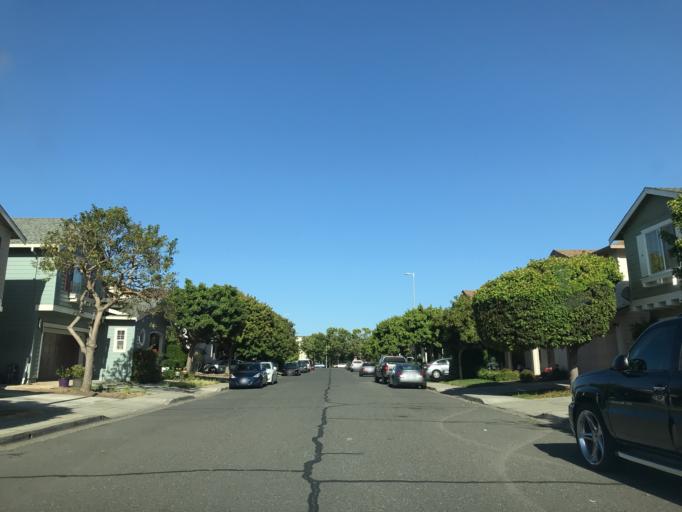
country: US
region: California
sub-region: San Mateo County
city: East Palo Alto
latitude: 37.4603
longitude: -122.1311
